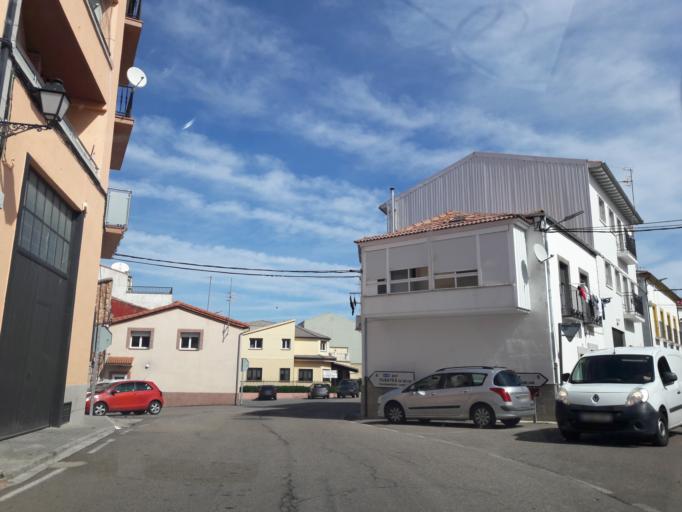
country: ES
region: Castille and Leon
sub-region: Provincia de Salamanca
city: Ledrada
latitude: 40.4672
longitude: -5.7209
